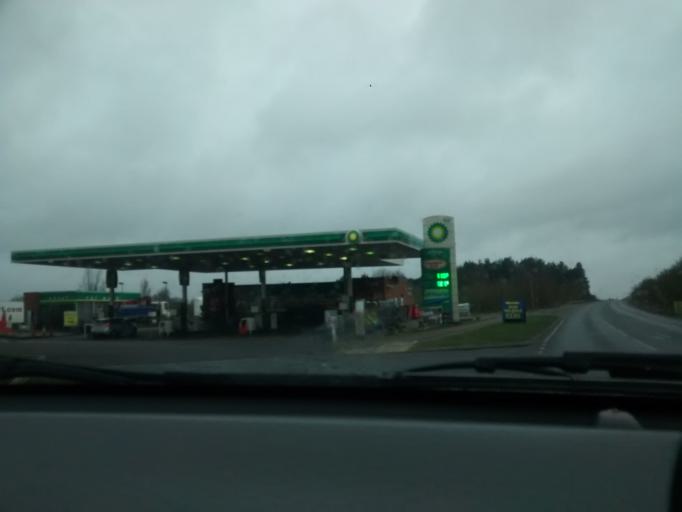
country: GB
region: England
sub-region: Suffolk
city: Stowmarket
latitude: 52.2050
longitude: 0.9792
